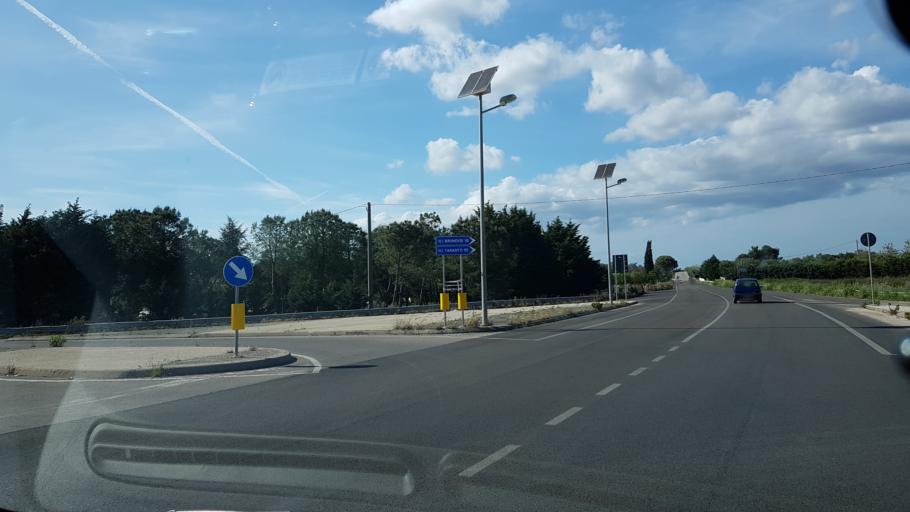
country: IT
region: Apulia
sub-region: Provincia di Brindisi
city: Mesagne
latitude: 40.5621
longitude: 17.7877
